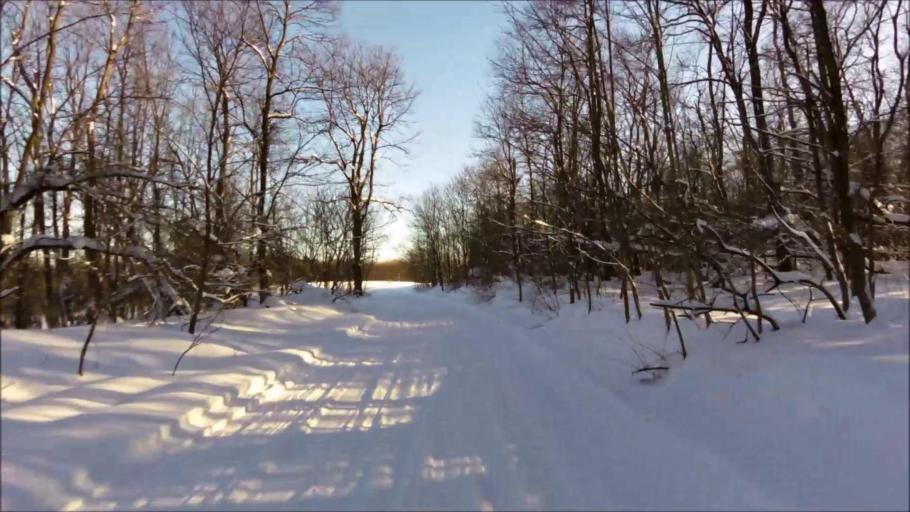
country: US
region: New York
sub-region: Chautauqua County
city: Mayville
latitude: 42.2527
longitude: -79.3865
